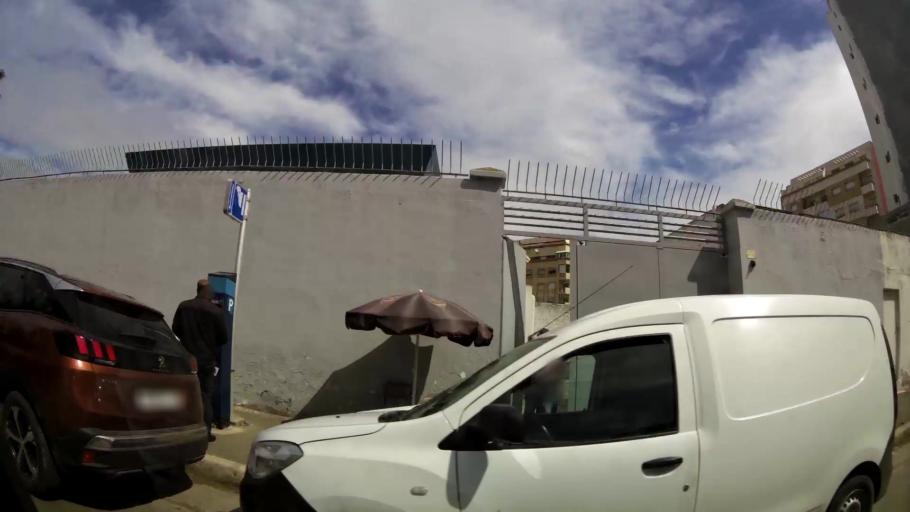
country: MA
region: Grand Casablanca
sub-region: Casablanca
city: Casablanca
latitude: 33.5903
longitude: -7.5986
